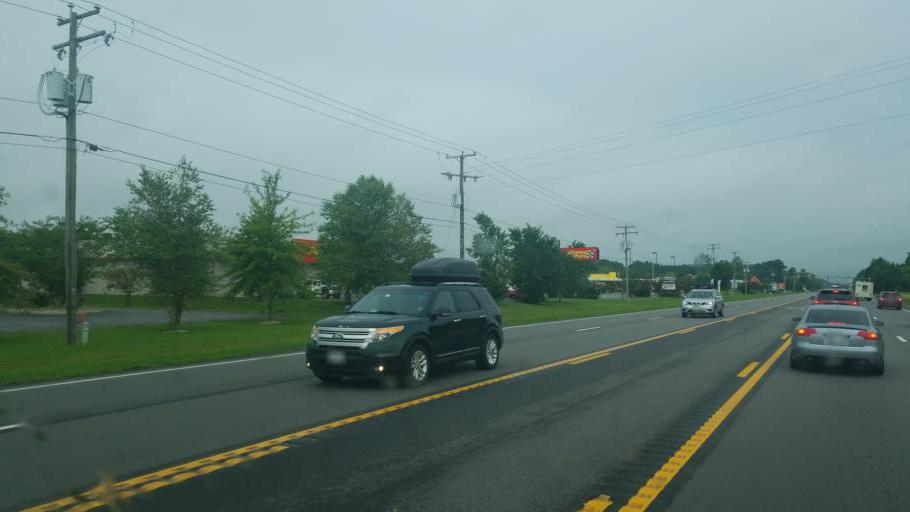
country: US
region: North Carolina
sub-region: Currituck County
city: Moyock
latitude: 36.5157
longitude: -76.1679
